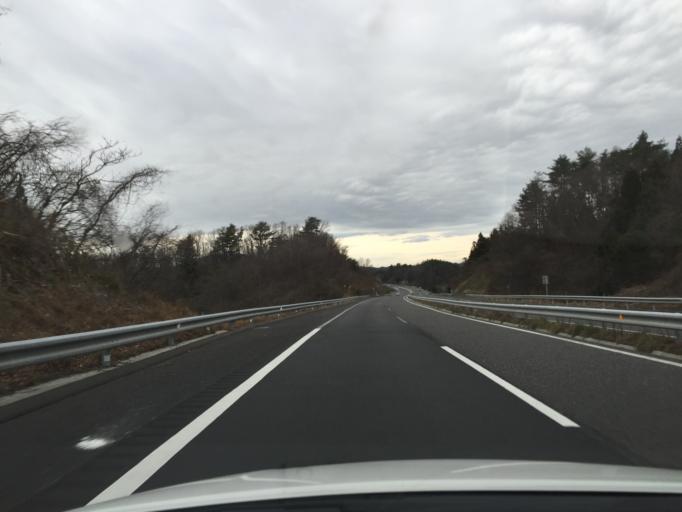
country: JP
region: Fukushima
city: Funehikimachi-funehiki
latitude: 37.3773
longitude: 140.5987
